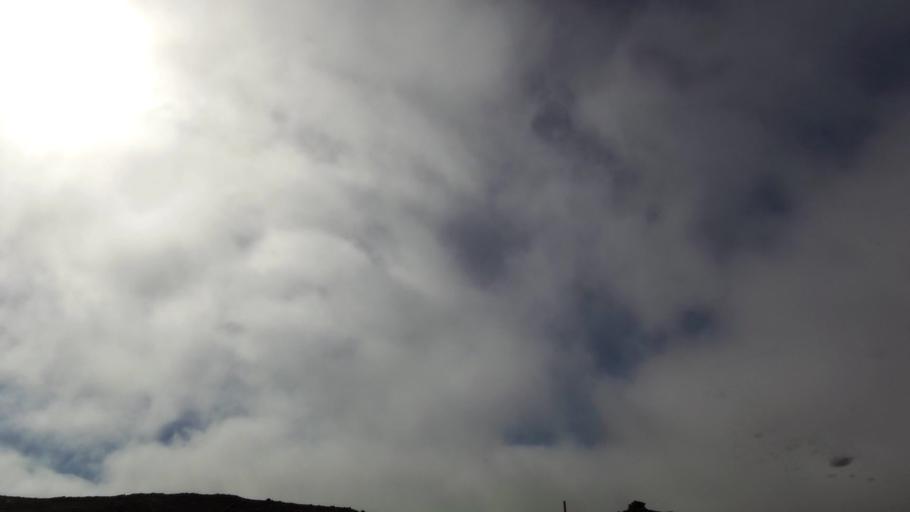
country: IS
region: West
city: Olafsvik
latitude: 65.5576
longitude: -24.2381
